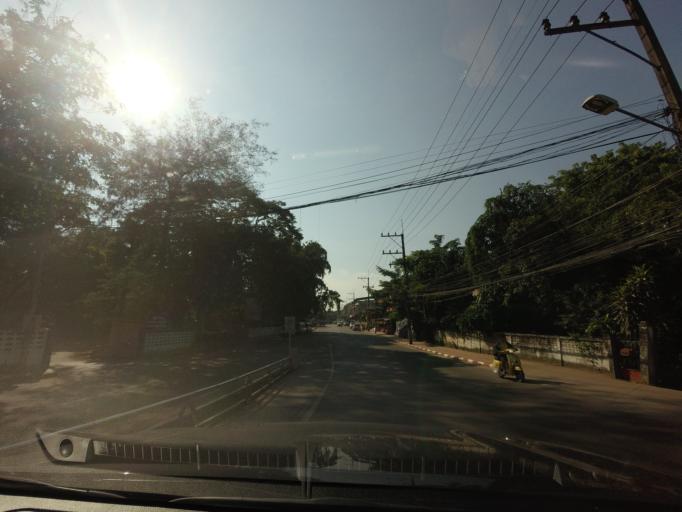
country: TH
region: Nan
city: Nan
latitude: 18.7763
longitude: 100.7781
